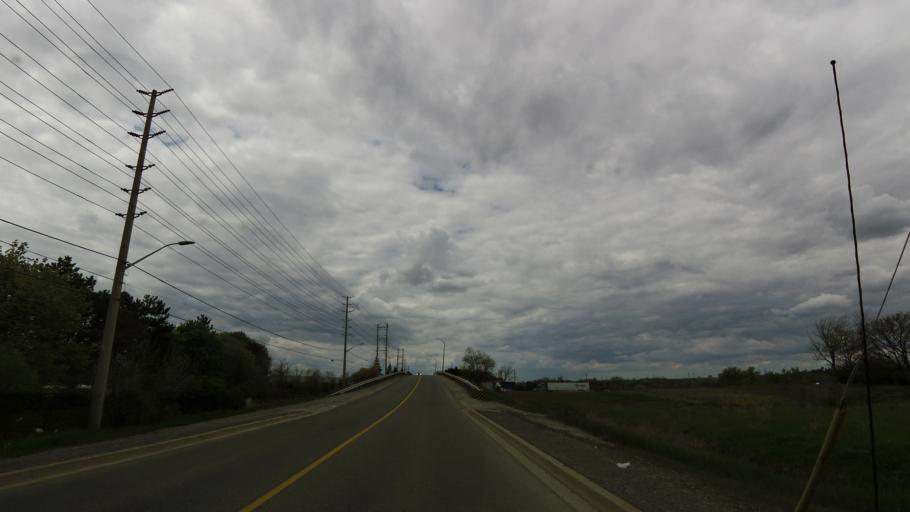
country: CA
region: Ontario
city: Mississauga
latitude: 43.6104
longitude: -79.7292
